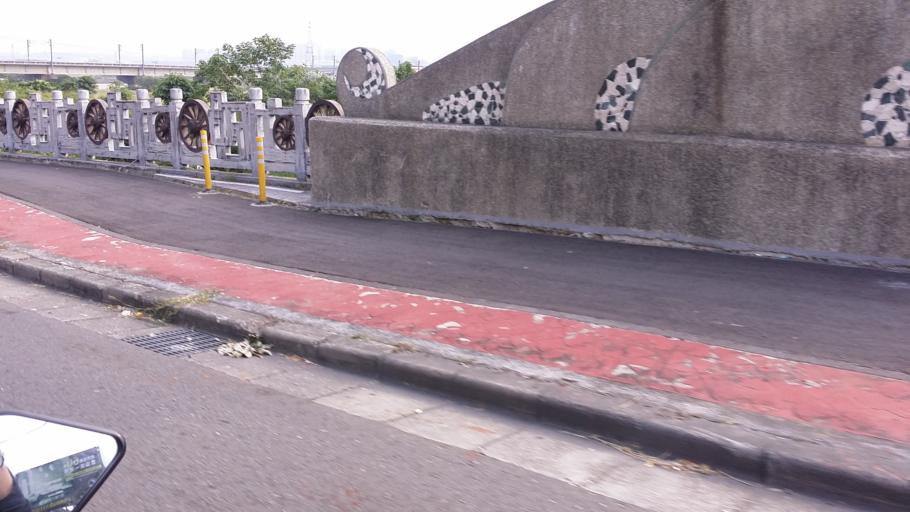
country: TW
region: Taiwan
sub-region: Hsinchu
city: Zhubei
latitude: 24.8255
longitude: 120.9976
